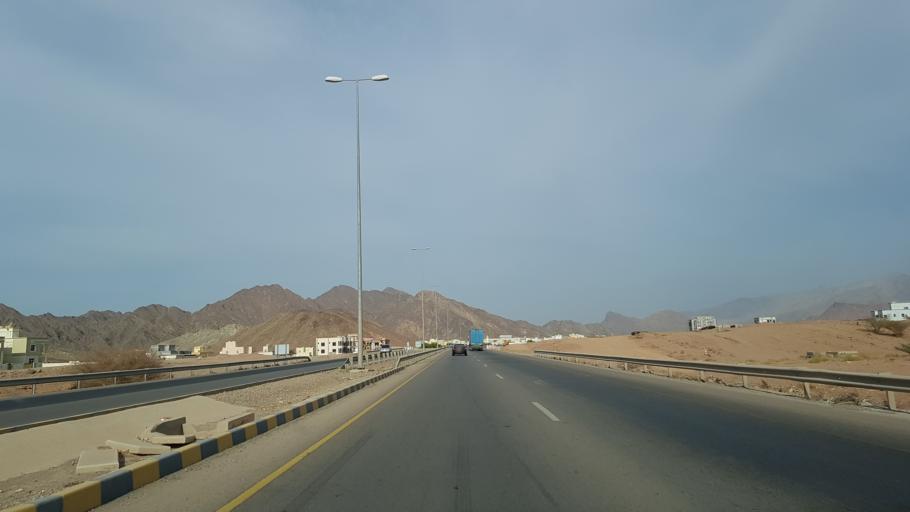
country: OM
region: Muhafazat ad Dakhiliyah
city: Bidbid
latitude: 23.4672
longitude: 58.1363
